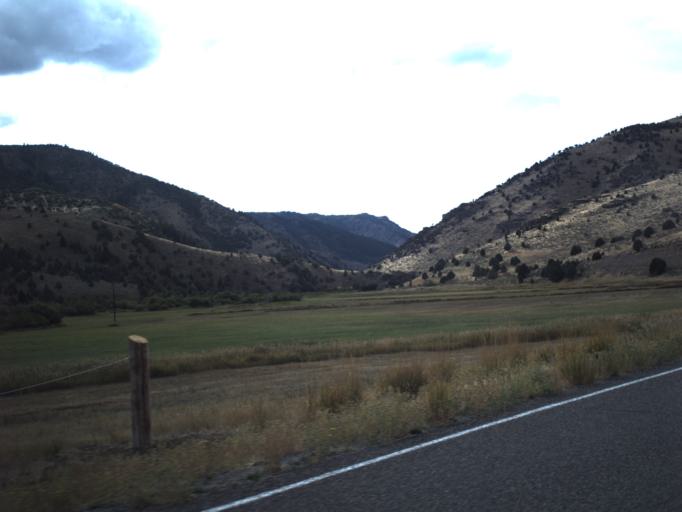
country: US
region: Utah
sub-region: Cache County
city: Millville
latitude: 41.6044
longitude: -111.5780
